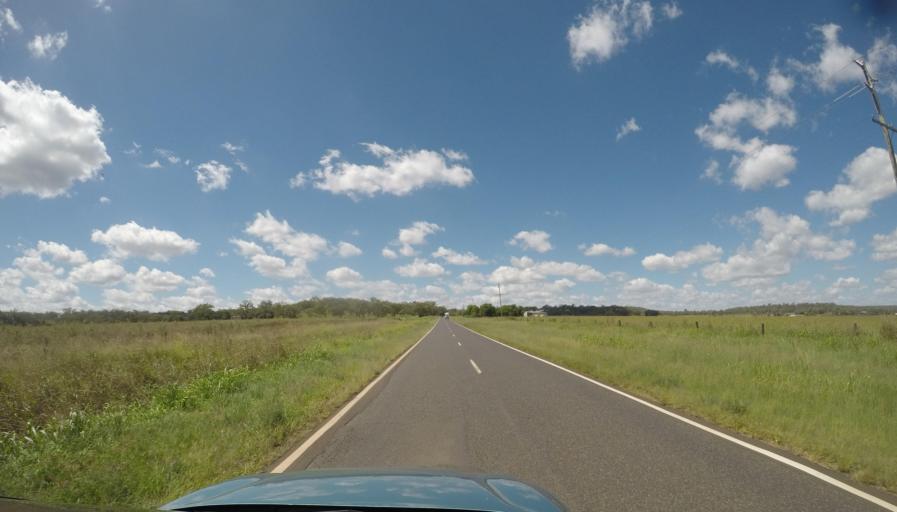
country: AU
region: Queensland
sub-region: Toowoomba
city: Oakey
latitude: -27.5414
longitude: 151.6579
